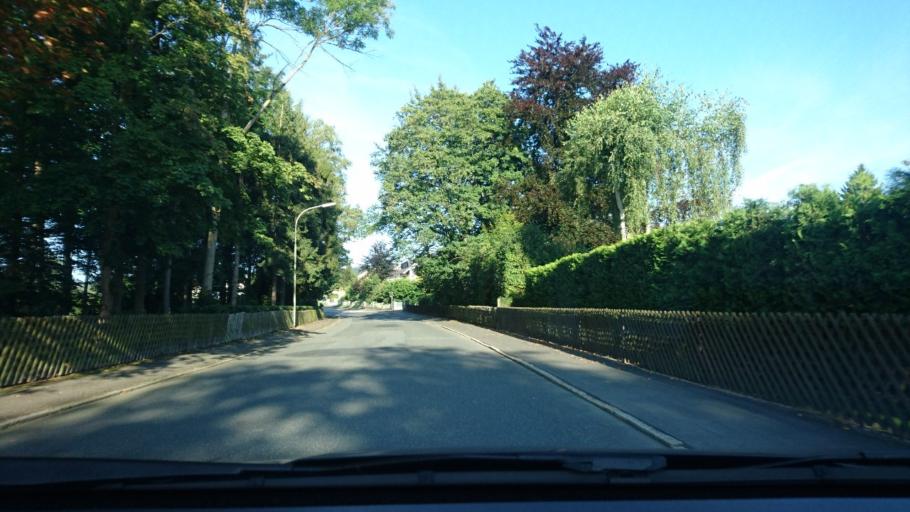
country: DE
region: Bavaria
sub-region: Upper Franconia
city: Naila
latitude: 50.3319
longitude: 11.7013
